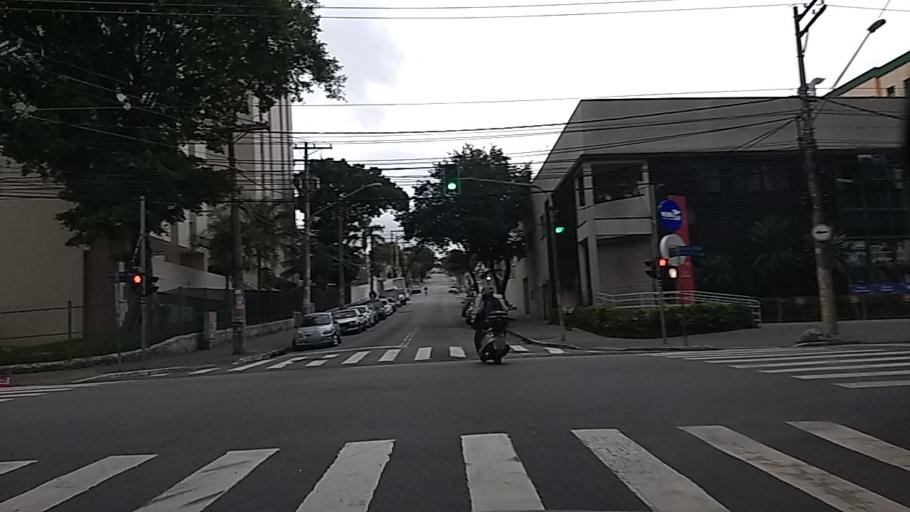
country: BR
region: Sao Paulo
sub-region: Sao Paulo
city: Sao Paulo
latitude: -23.5069
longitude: -46.6013
